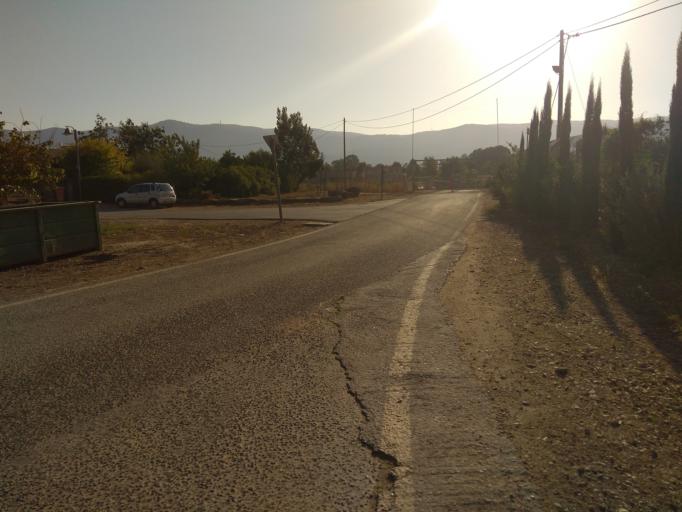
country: IL
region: Northern District
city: Qiryat Shemona
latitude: 33.2210
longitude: 35.6185
